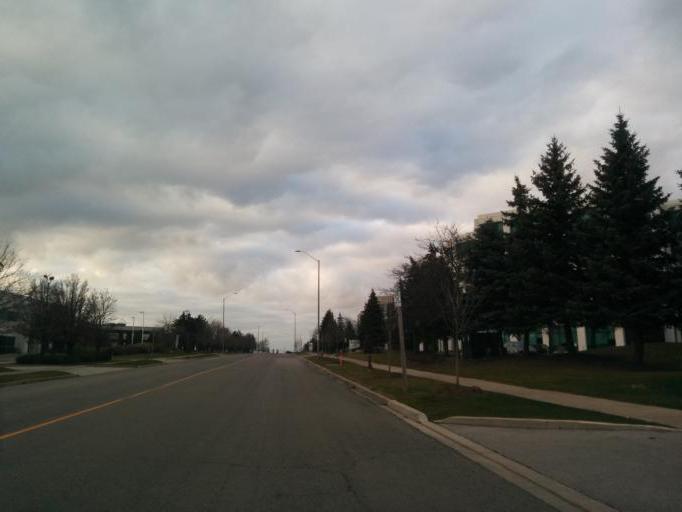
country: CA
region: Ontario
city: Etobicoke
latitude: 43.6593
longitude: -79.6052
